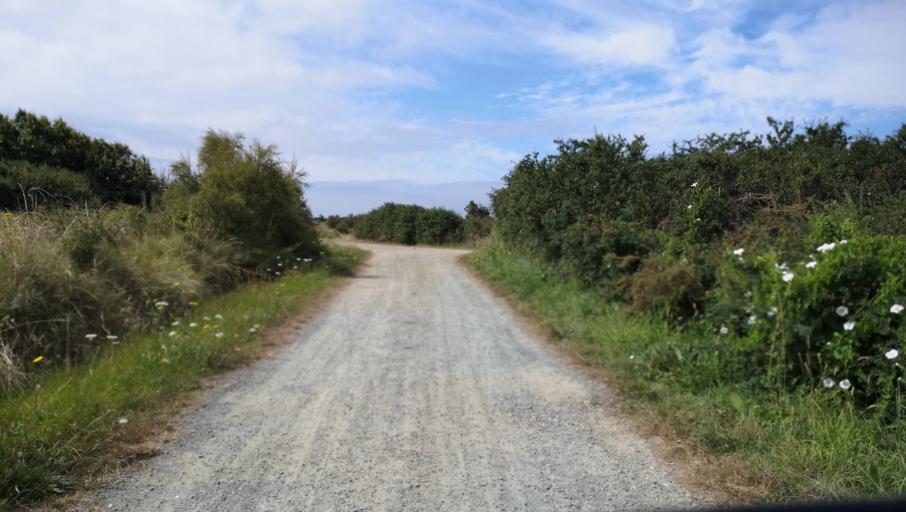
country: FR
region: Pays de la Loire
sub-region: Departement de la Vendee
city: Olonne-sur-Mer
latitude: 46.5678
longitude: -1.7863
